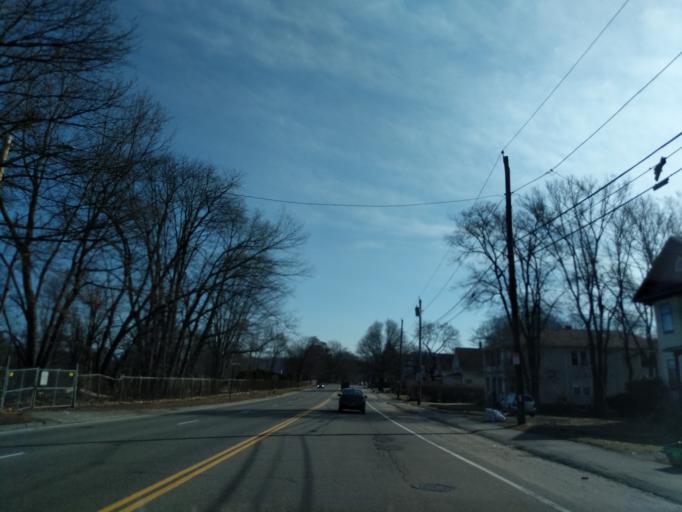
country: US
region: Massachusetts
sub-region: Worcester County
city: Auburn
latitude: 42.2320
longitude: -71.8325
